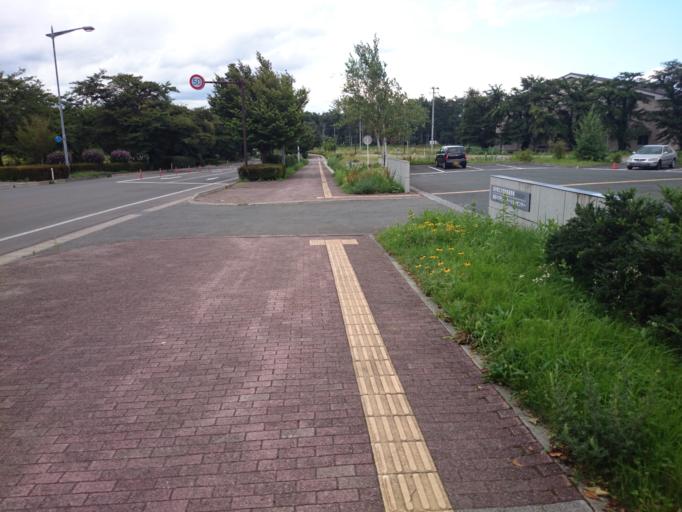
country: JP
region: Iwate
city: Morioka-shi
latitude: 39.8001
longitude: 141.1380
